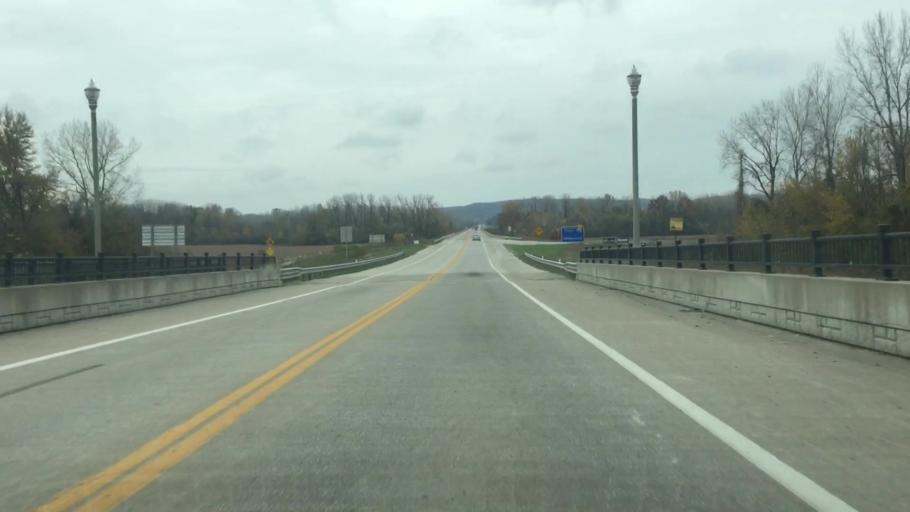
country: US
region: Missouri
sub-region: Gasconade County
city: Hermann
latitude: 38.7129
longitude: -91.4401
